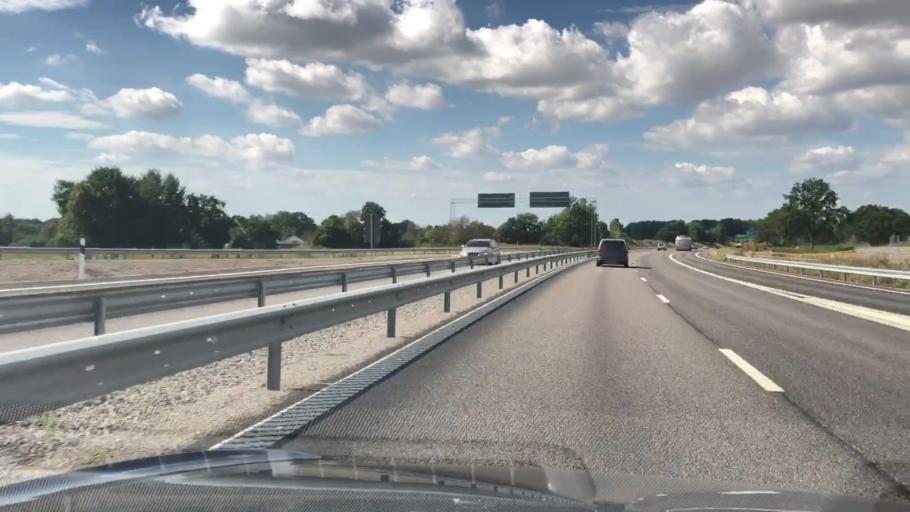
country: SE
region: Kalmar
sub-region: Kalmar Kommun
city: Rinkabyholm
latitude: 56.6668
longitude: 16.2794
